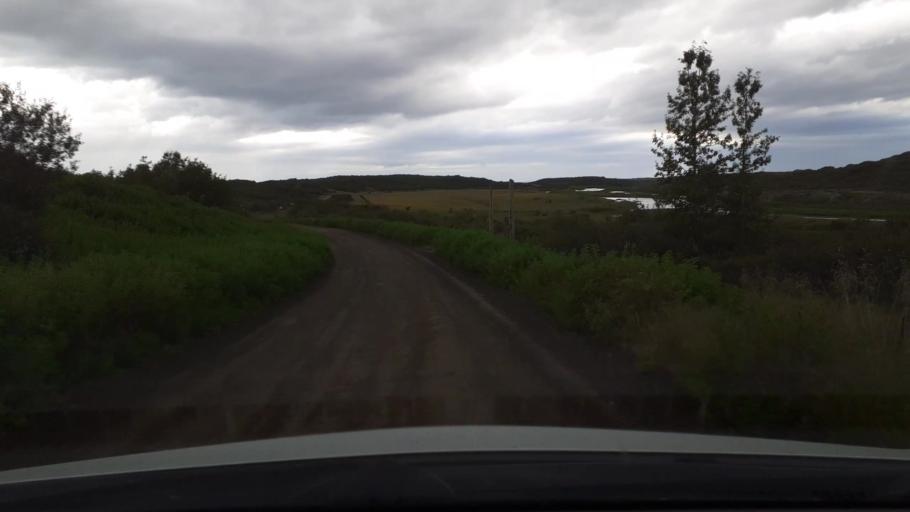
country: IS
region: West
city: Borgarnes
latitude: 64.6162
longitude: -21.9491
